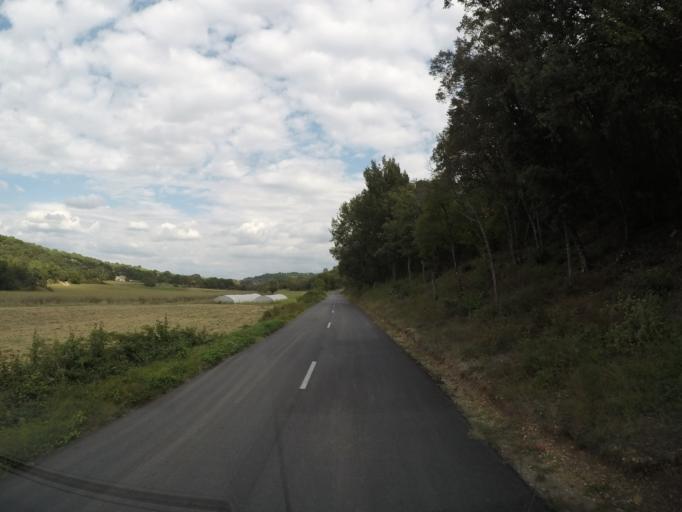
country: FR
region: Provence-Alpes-Cote d'Azur
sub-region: Departement des Alpes-de-Haute-Provence
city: Valensole
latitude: 43.8155
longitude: 5.9593
